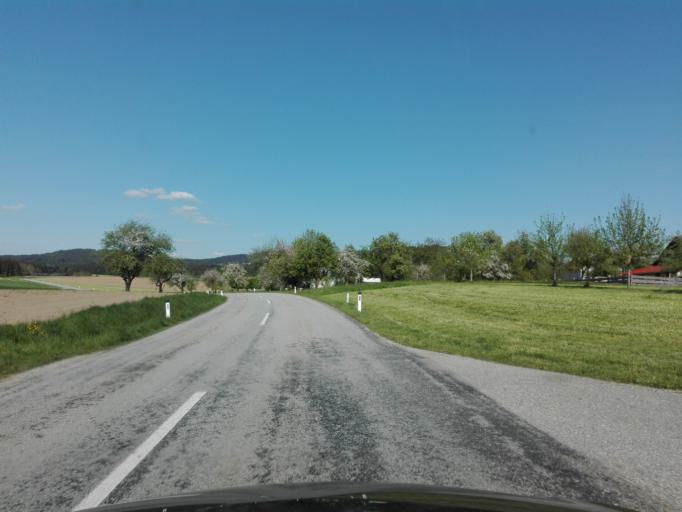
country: DE
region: Bavaria
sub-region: Lower Bavaria
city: Obernzell
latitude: 48.5004
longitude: 13.6018
